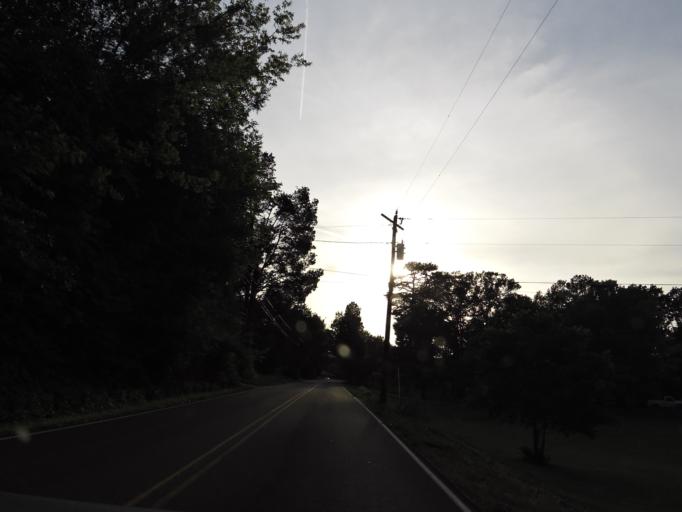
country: US
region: Tennessee
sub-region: Sevier County
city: Seymour
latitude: 35.9054
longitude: -83.8063
